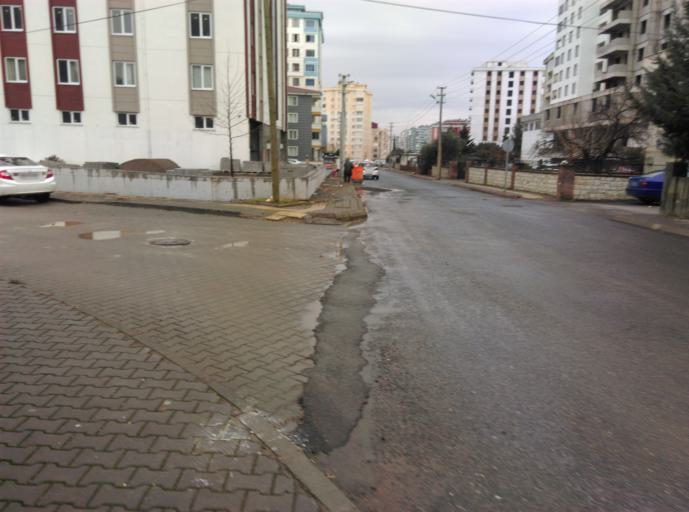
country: TR
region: Kahramanmaras
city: Kahramanmaras
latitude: 37.5836
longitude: 36.8955
